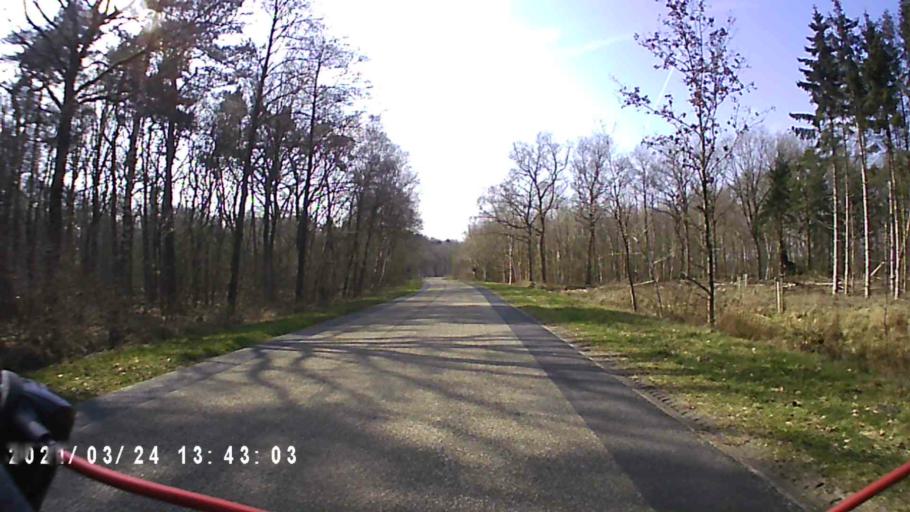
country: NL
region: Groningen
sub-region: Gemeente Grootegast
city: Grootegast
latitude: 53.0867
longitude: 6.2735
